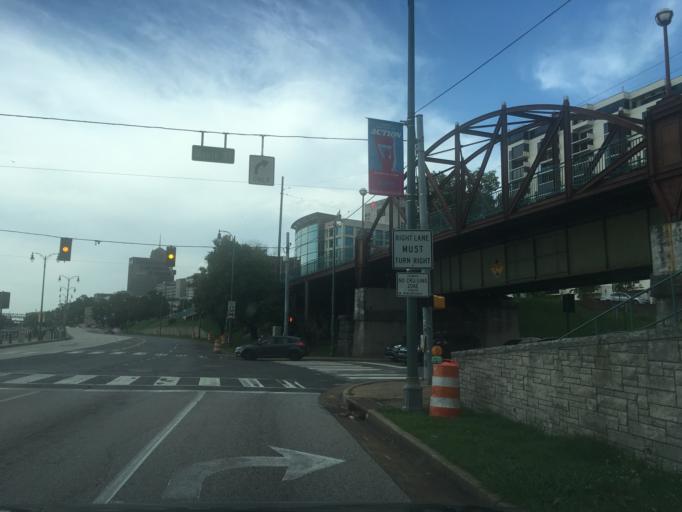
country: US
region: Tennessee
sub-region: Shelby County
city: Memphis
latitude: 35.1410
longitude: -90.0581
